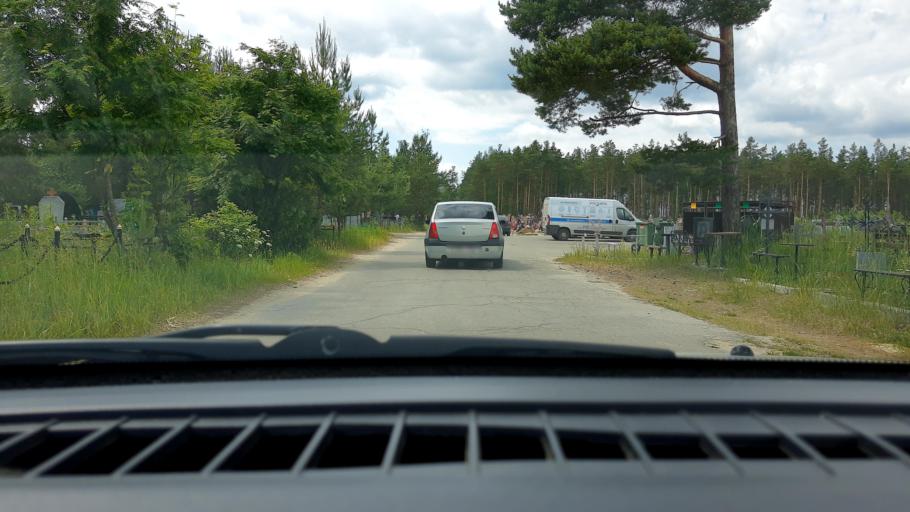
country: RU
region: Nizjnij Novgorod
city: Gorbatovka
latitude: 56.3605
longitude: 43.7624
